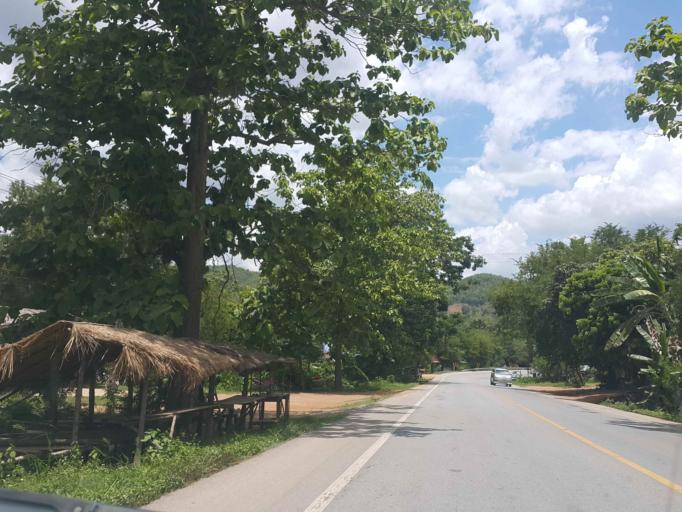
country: TH
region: Nan
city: Wiang Sa
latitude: 18.5168
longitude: 100.6006
